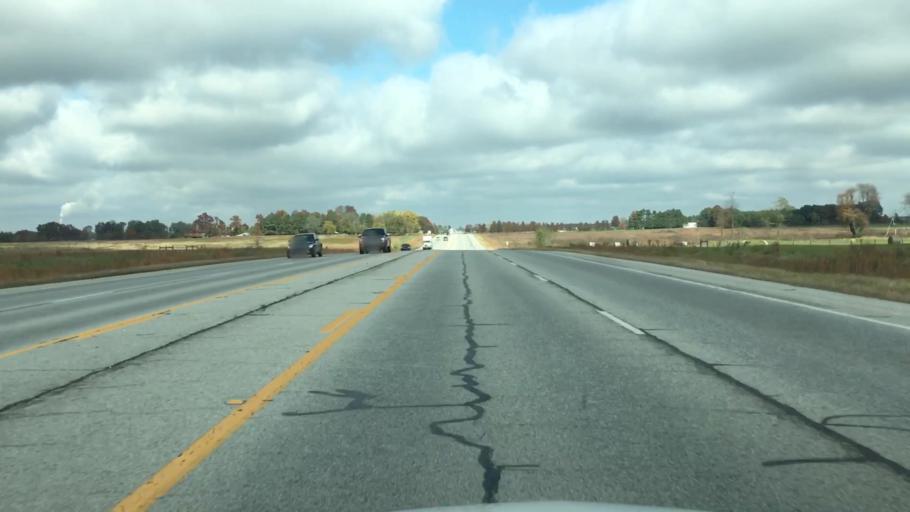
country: US
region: Arkansas
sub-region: Benton County
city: Siloam Springs
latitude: 36.1999
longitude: -94.4958
